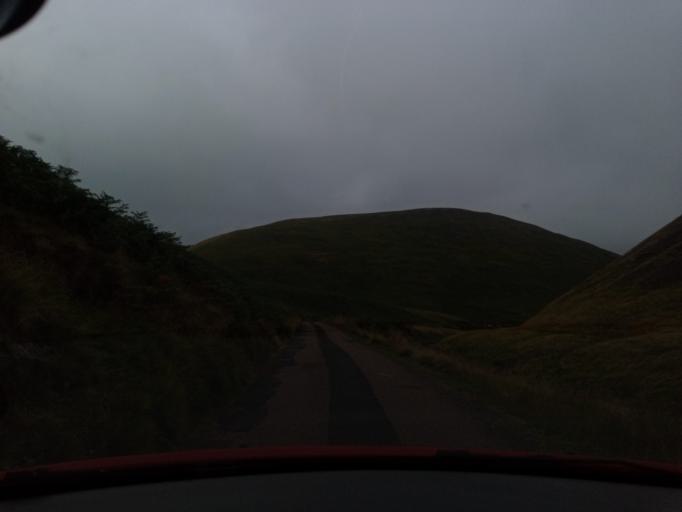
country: GB
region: England
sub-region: Northumberland
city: Rochester
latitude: 55.3963
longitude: -2.2284
